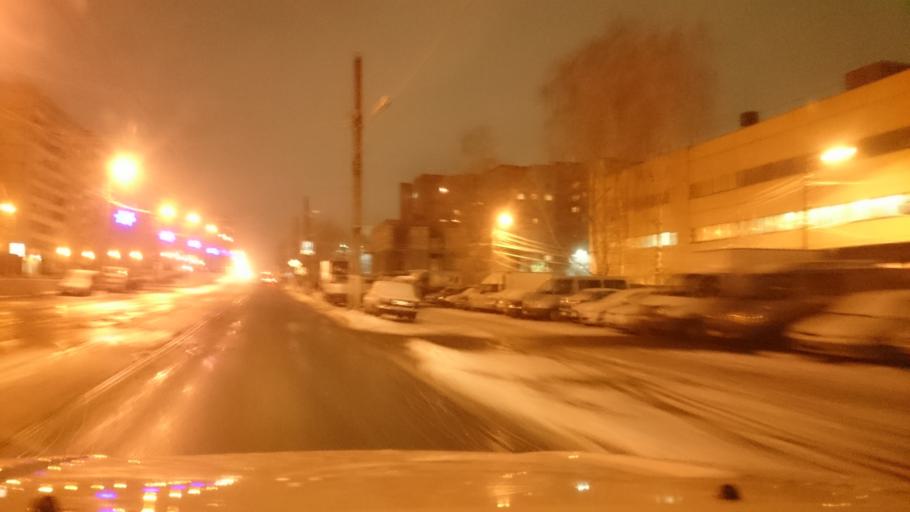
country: RU
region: Tula
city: Tula
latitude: 54.2146
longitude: 37.6126
